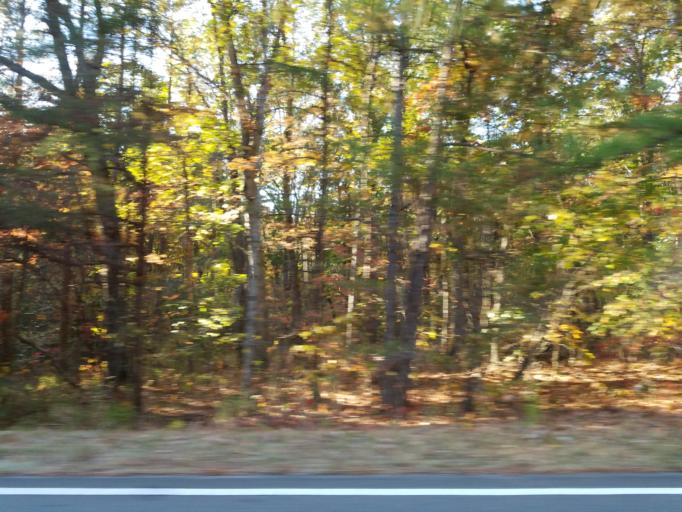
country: US
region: Georgia
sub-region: Pickens County
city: Jasper
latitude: 34.5499
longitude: -84.4693
